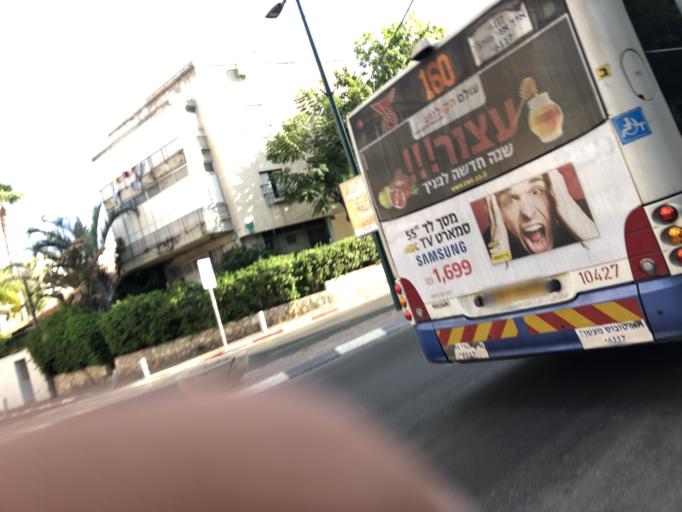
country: IL
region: Tel Aviv
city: Ramat Gan
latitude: 32.0832
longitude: 34.8211
